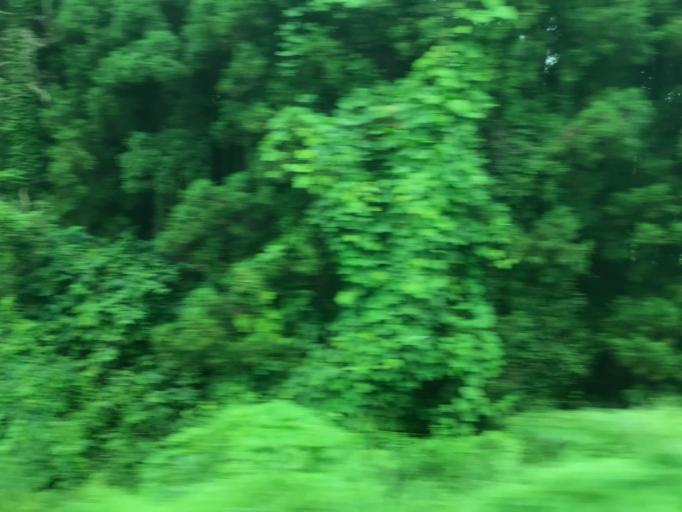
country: JP
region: Fukushima
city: Ishikawa
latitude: 37.1408
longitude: 140.2653
